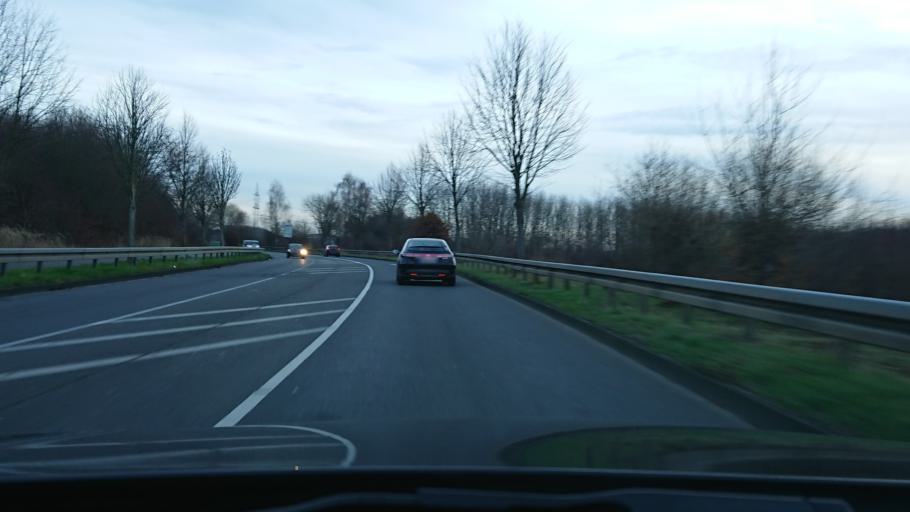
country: DE
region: North Rhine-Westphalia
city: Monheim am Rhein
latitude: 51.0359
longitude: 6.8798
